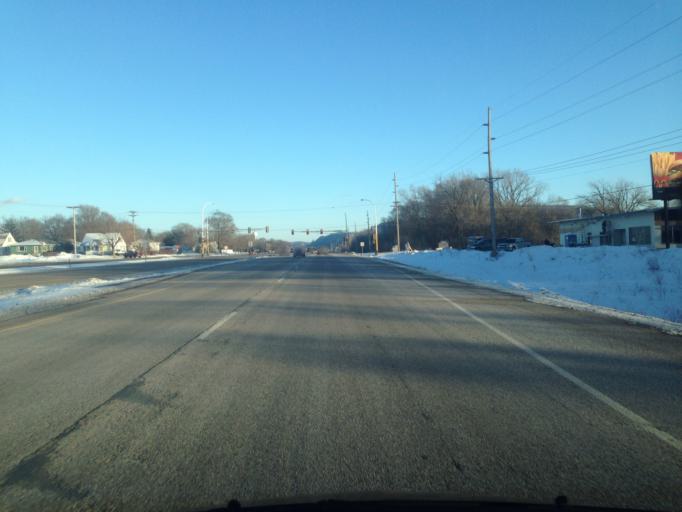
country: US
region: Minnesota
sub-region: Winona County
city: Goodview
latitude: 44.0608
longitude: -91.7046
